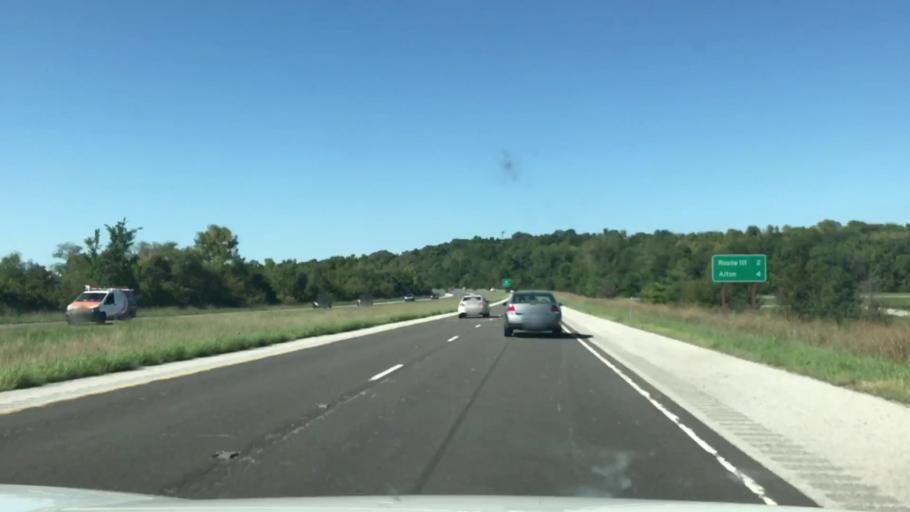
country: US
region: Illinois
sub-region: Madison County
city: South Roxana
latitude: 38.8357
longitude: -90.0435
